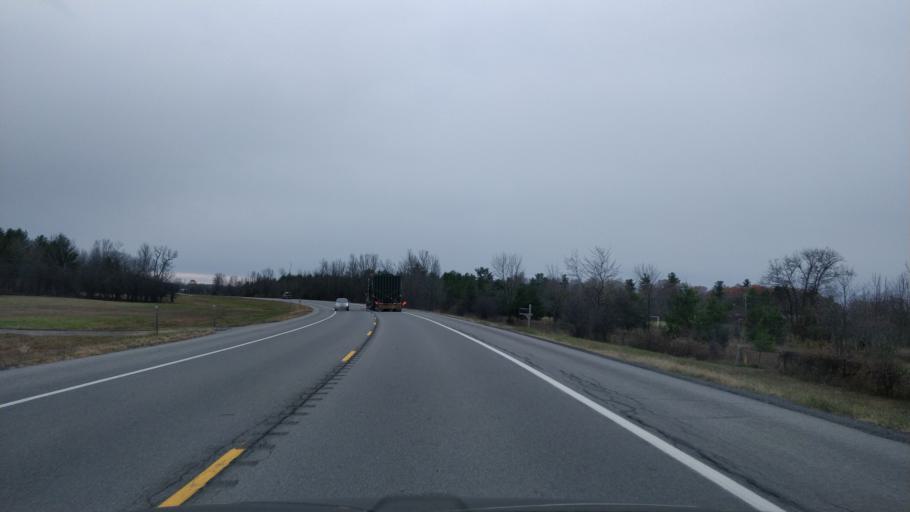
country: CA
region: Ontario
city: Brockville
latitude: 44.5898
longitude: -75.6405
